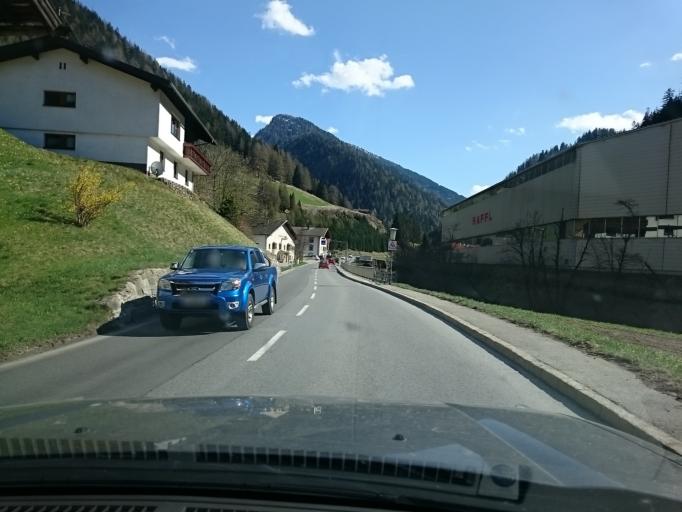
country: AT
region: Tyrol
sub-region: Politischer Bezirk Innsbruck Land
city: Steinach am Brenner
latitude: 47.0720
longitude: 11.4847
